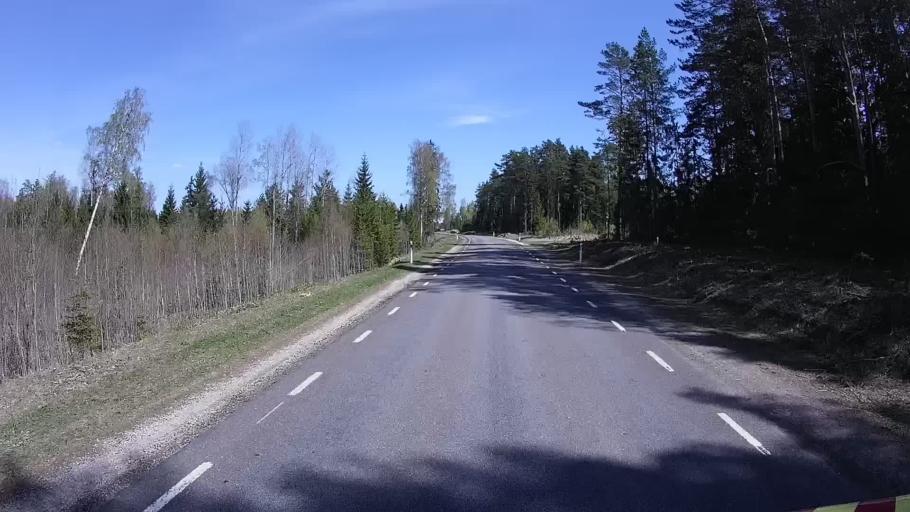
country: EE
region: Harju
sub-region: Nissi vald
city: Turba
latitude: 59.1022
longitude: 24.0283
